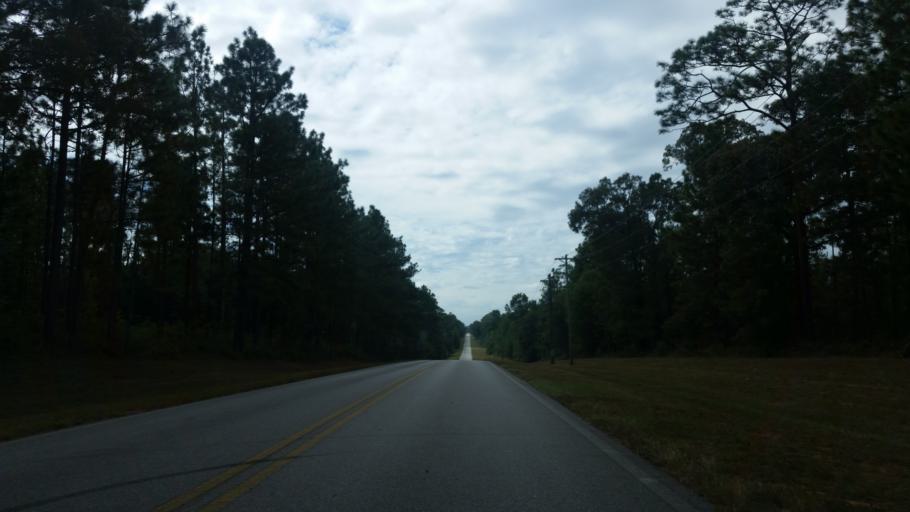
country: US
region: Florida
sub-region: Santa Rosa County
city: Point Baker
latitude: 30.8494
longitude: -86.8803
